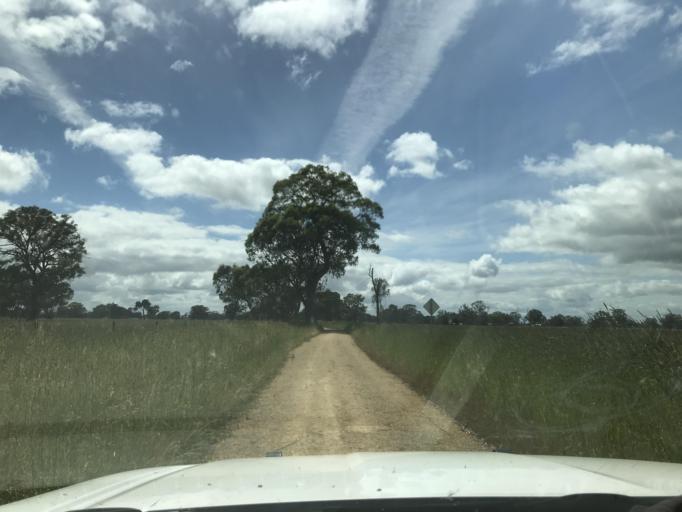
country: AU
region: South Australia
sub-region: Naracoorte and Lucindale
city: Naracoorte
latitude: -37.0183
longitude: 141.0901
